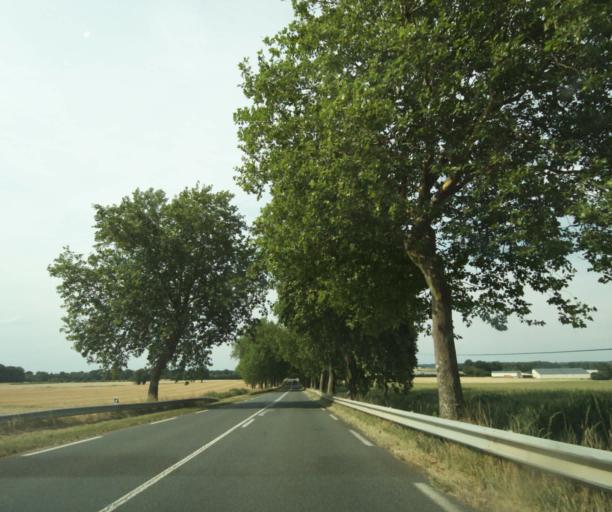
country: FR
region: Centre
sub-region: Departement d'Indre-et-Loire
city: Saint-Christophe-sur-le-Nais
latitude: 47.6207
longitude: 0.5042
